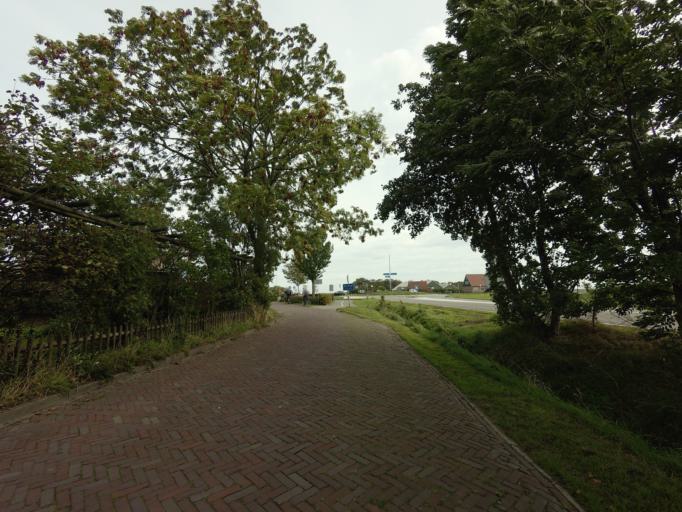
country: NL
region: North Holland
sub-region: Gemeente Texel
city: Den Burg
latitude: 53.0719
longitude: 4.8242
